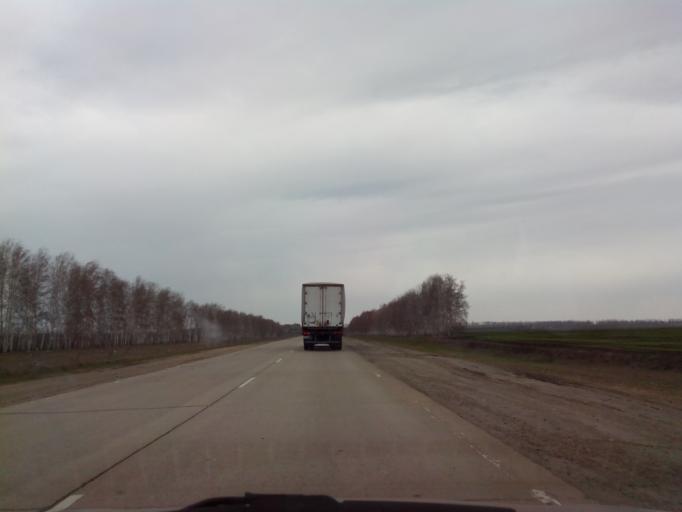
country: RU
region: Tambov
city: Pokrovo-Prigorodnoye
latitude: 52.6484
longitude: 41.3409
